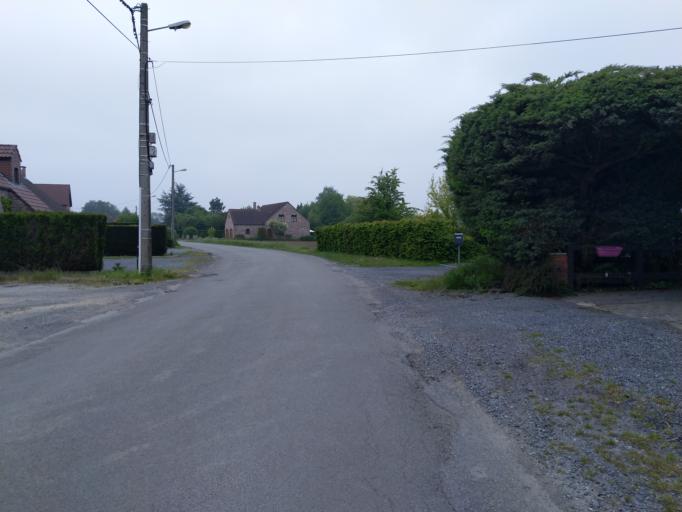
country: BE
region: Wallonia
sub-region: Province du Hainaut
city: Jurbise
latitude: 50.4890
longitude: 3.9186
